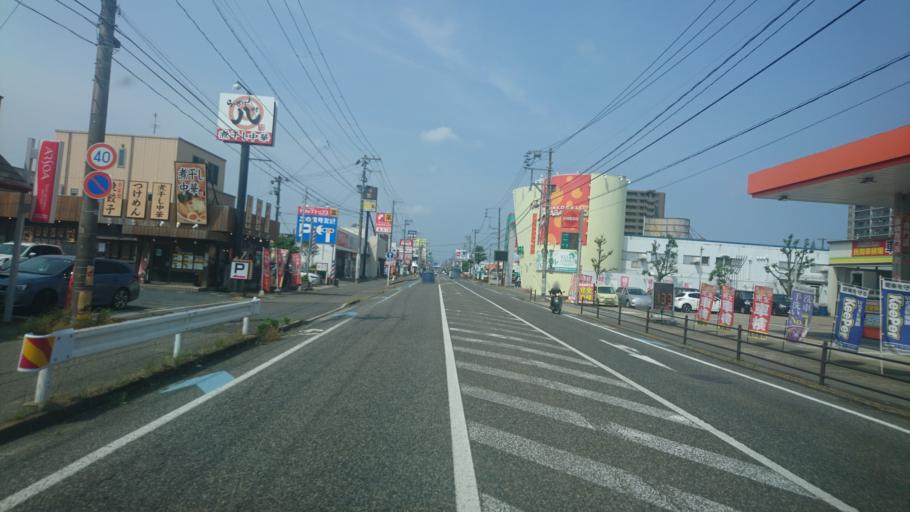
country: JP
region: Niigata
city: Niigata-shi
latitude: 37.9062
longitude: 139.0536
